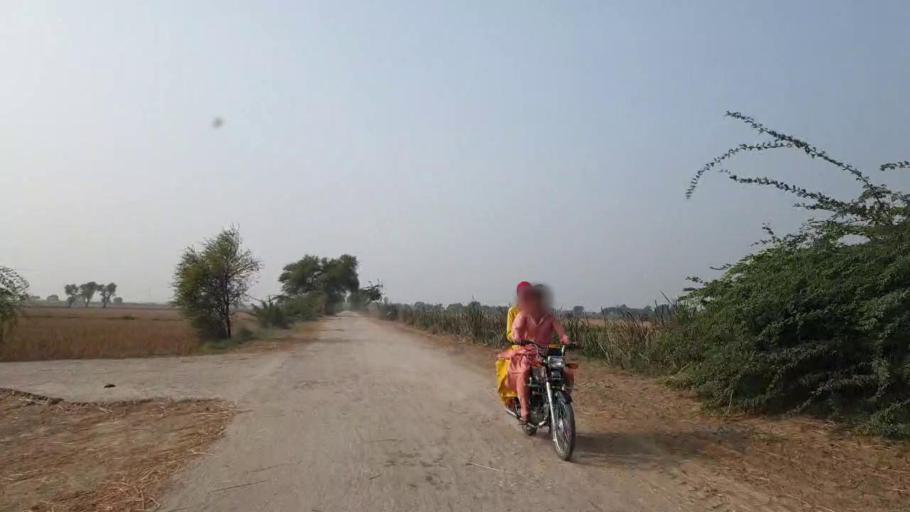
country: PK
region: Sindh
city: Matli
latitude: 25.0673
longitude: 68.6008
